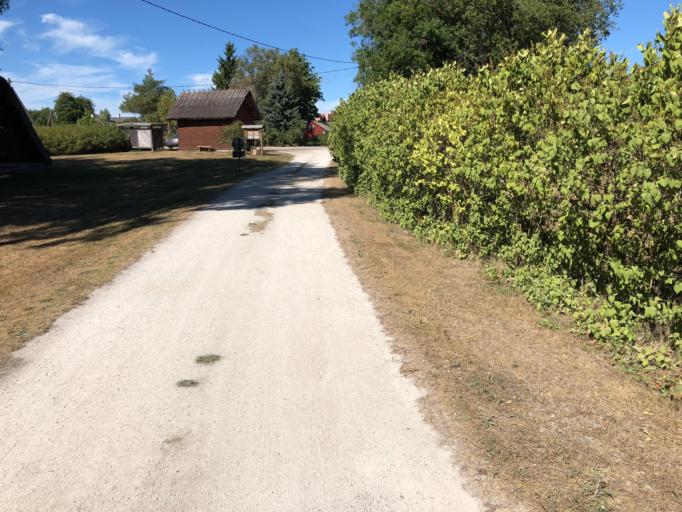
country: EE
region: Laeaene
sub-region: Haapsalu linn
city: Haapsalu
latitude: 58.7727
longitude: 23.5478
